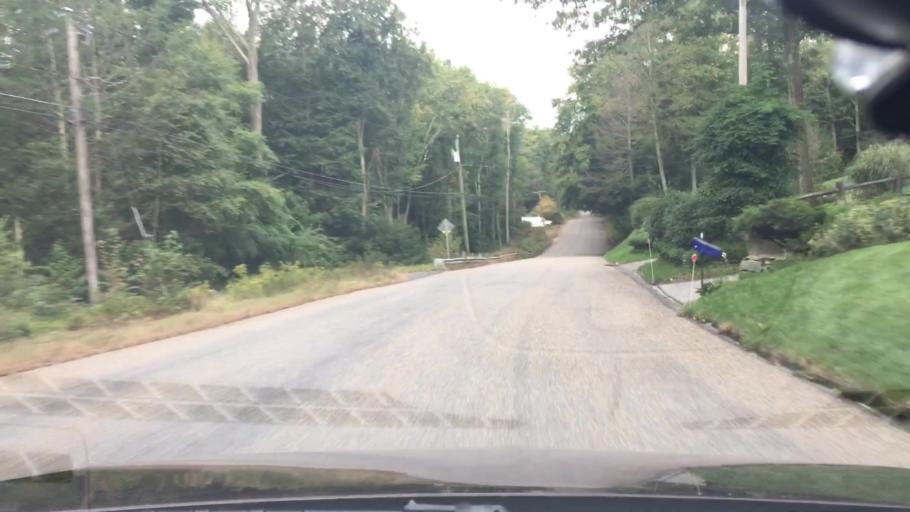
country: US
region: Connecticut
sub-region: Tolland County
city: Stafford
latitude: 41.9895
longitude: -72.3090
